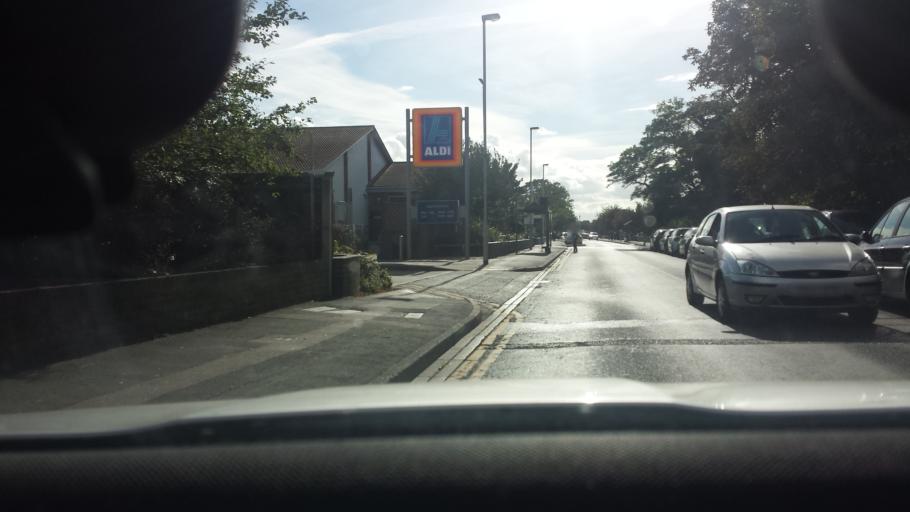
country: GB
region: England
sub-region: Kent
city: Swanley
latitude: 51.3972
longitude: 0.1721
